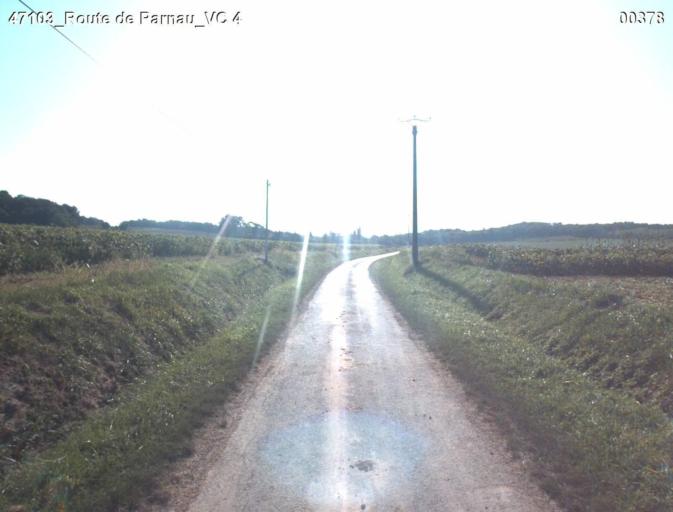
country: FR
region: Aquitaine
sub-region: Departement du Lot-et-Garonne
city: Nerac
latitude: 44.0832
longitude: 0.3334
